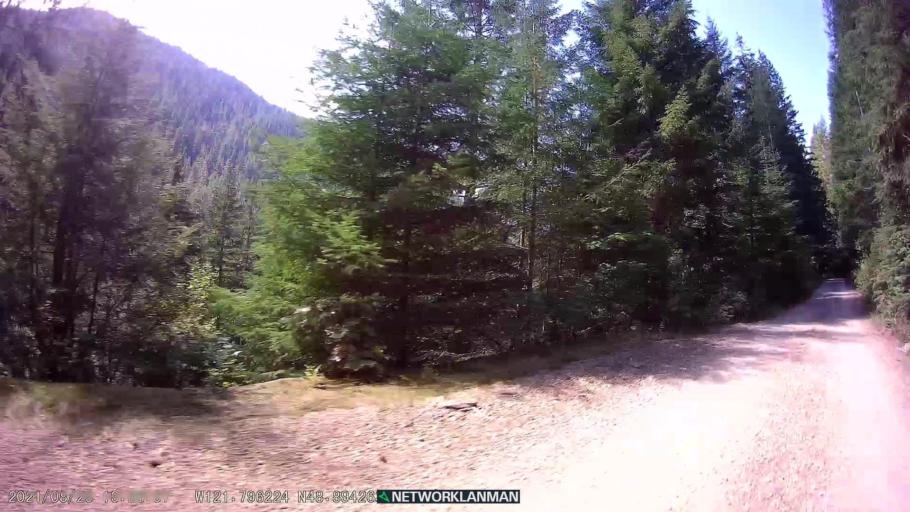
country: CA
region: British Columbia
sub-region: Fraser Valley Regional District
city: Chilliwack
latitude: 48.8944
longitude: -121.7963
